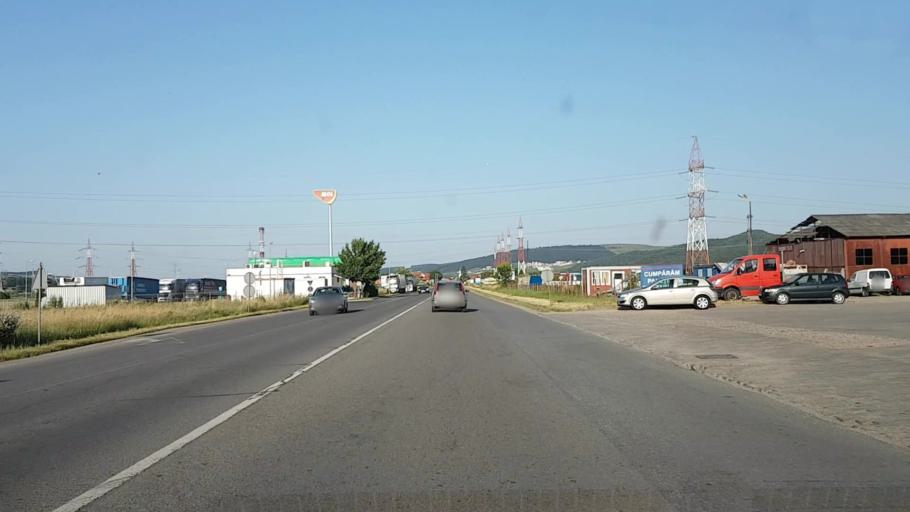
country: RO
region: Cluj
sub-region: Comuna Floresti
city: Luna de Sus
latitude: 46.7444
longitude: 23.4563
